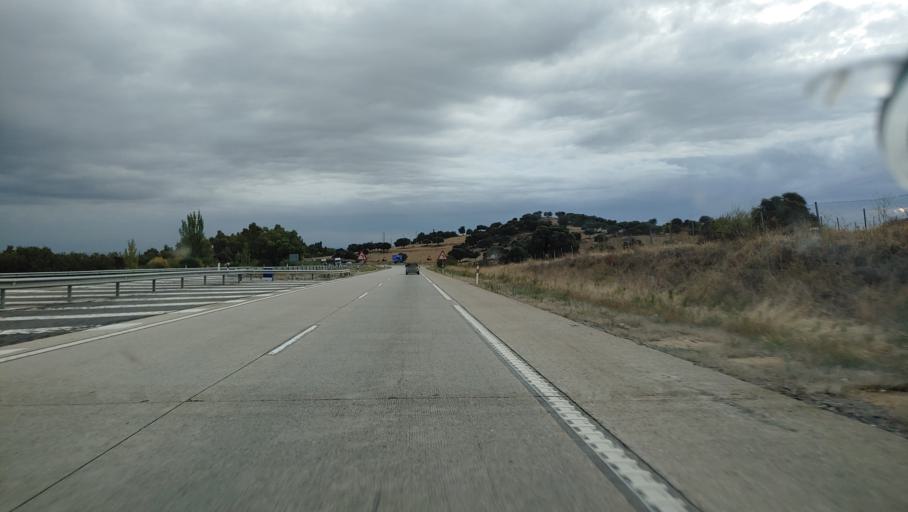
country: ES
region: Andalusia
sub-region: Provincia de Jaen
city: Santa Elena
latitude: 38.3111
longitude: -3.5746
